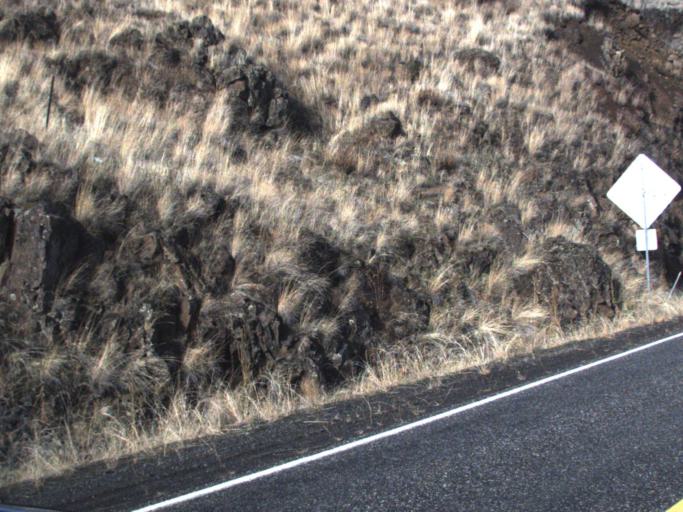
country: US
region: Washington
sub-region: Asotin County
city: Asotin
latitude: 45.9999
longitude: -117.2812
